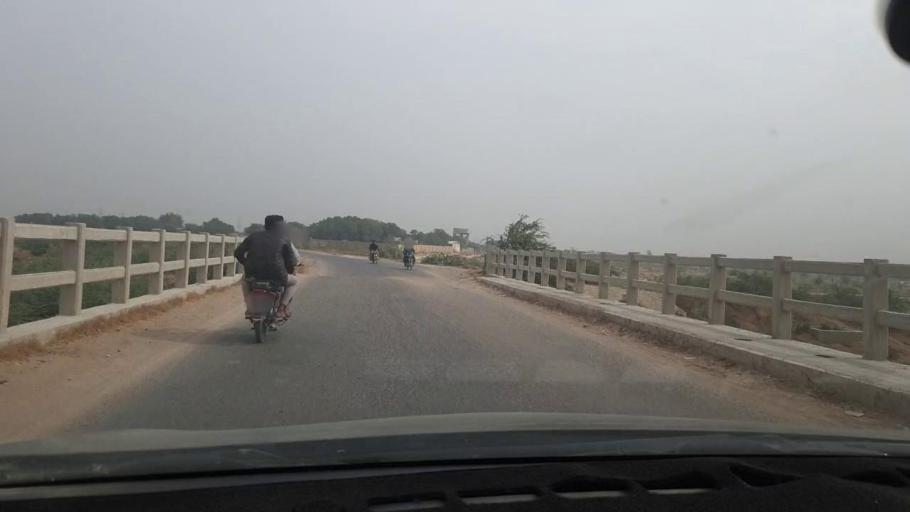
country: PK
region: Sindh
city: Malir Cantonment
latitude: 24.9142
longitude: 67.2675
